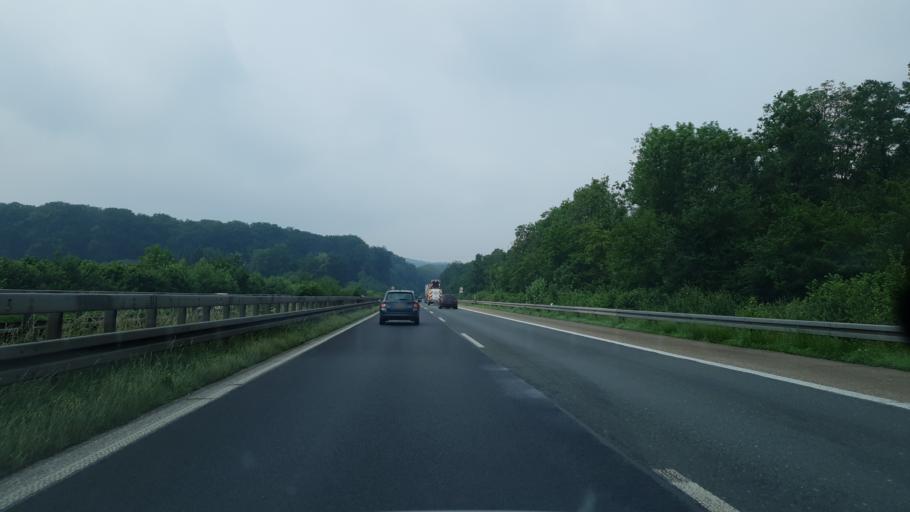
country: DE
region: North Rhine-Westphalia
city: Sprockhovel
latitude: 51.3746
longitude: 7.2677
